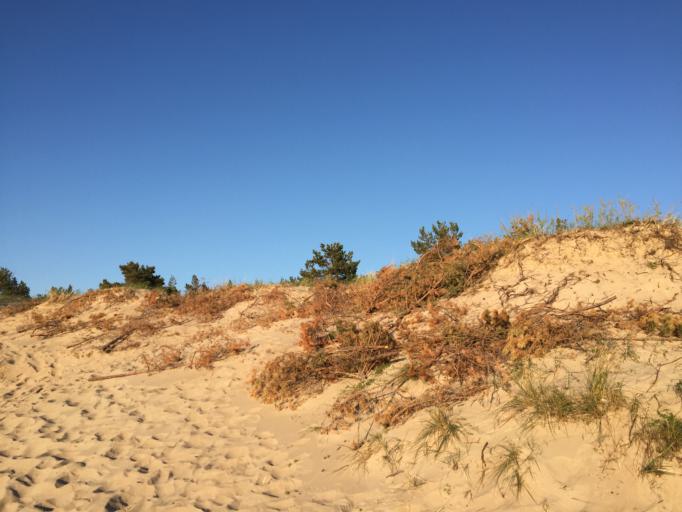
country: LV
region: Carnikava
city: Carnikava
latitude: 57.1443
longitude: 24.2423
